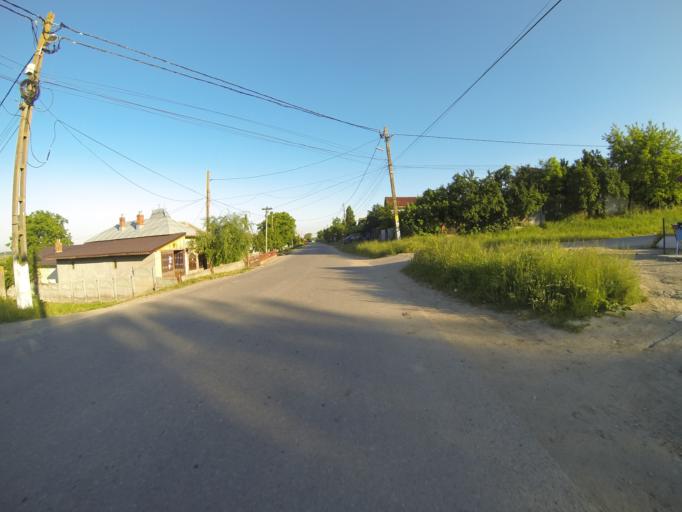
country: RO
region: Dolj
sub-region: Comuna Tuglui
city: Tuglui
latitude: 44.2067
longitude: 23.7964
